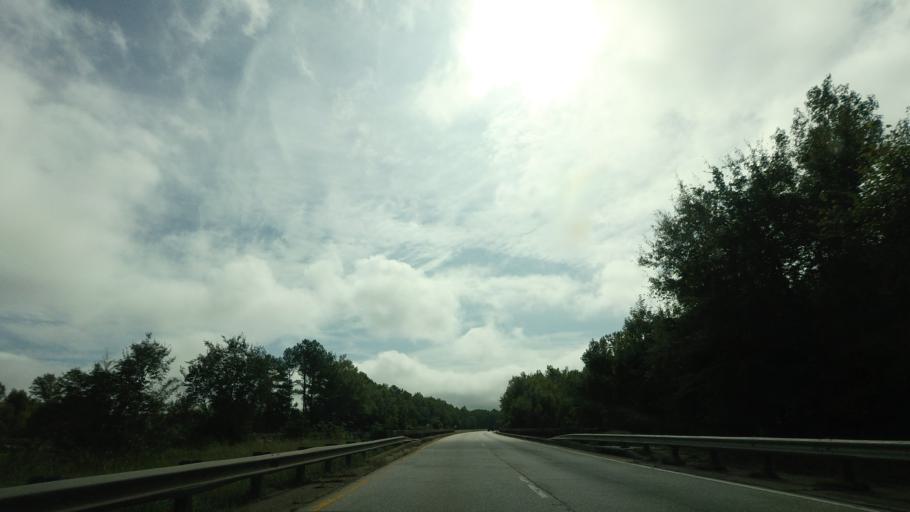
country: US
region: Georgia
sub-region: Bibb County
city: Macon
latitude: 32.8157
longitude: -83.5826
